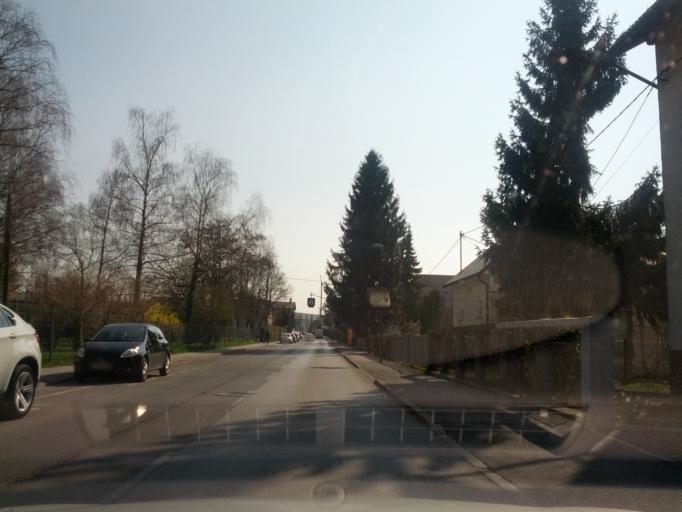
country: SI
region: Ljubljana
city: Ljubljana
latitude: 46.0727
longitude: 14.5378
